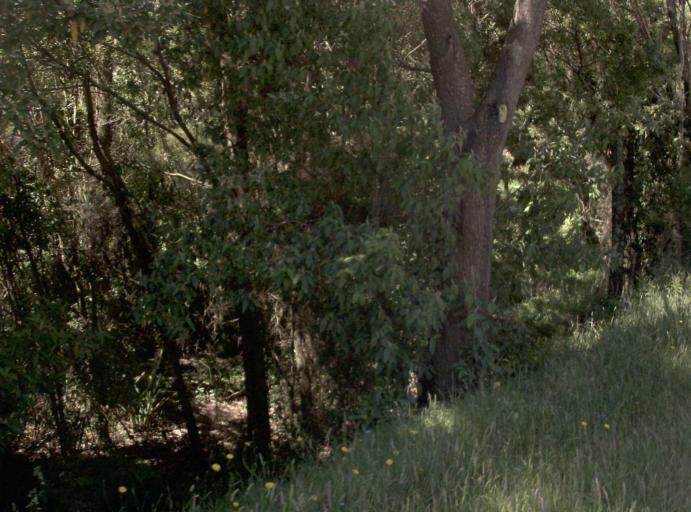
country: AU
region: Victoria
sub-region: Latrobe
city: Morwell
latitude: -38.6899
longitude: 146.1346
